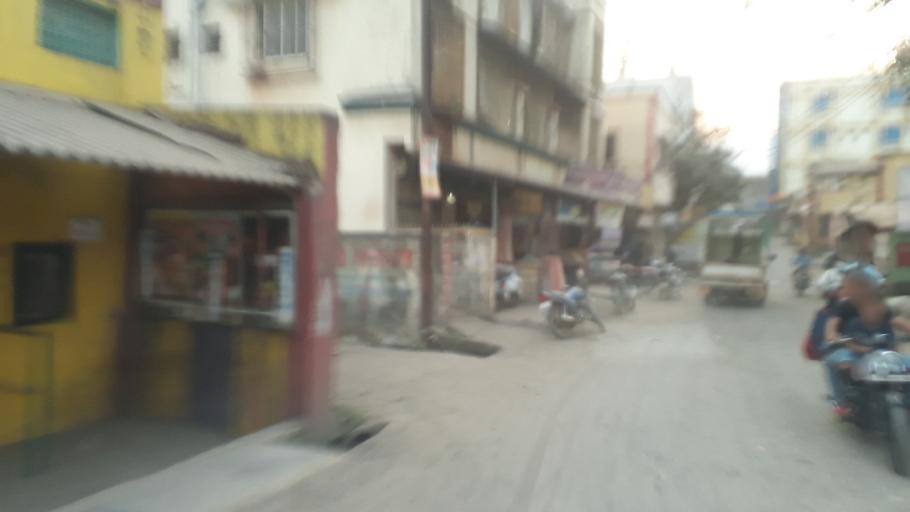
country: IN
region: Maharashtra
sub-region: Raigarh
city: Neral
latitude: 19.0230
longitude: 73.3173
